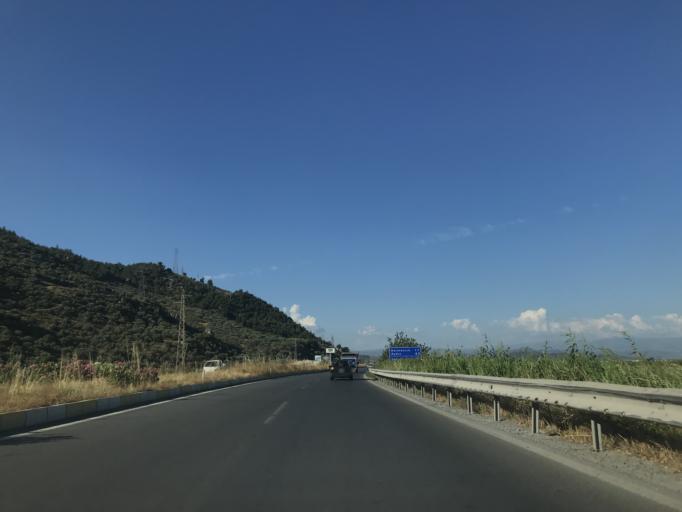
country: TR
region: Aydin
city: Soeke
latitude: 37.7993
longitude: 27.4717
